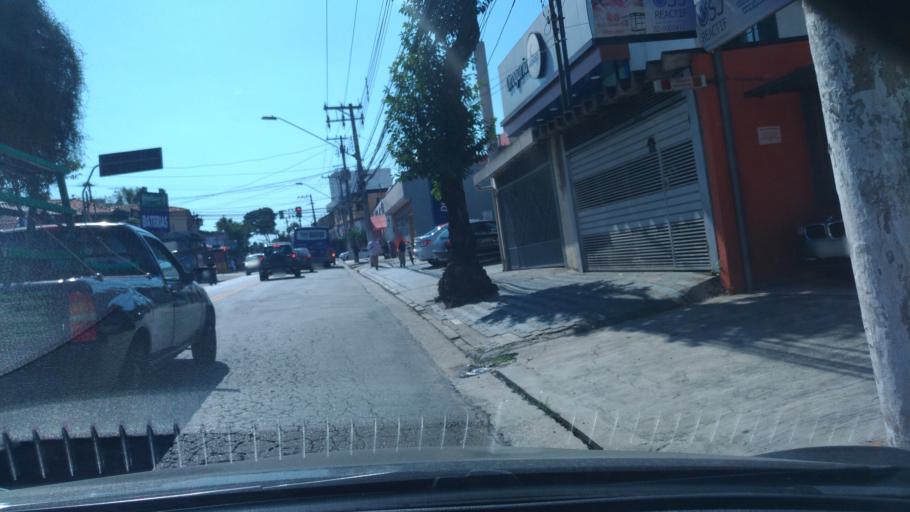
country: BR
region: Sao Paulo
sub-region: Santo Andre
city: Santo Andre
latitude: -23.6663
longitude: -46.5447
